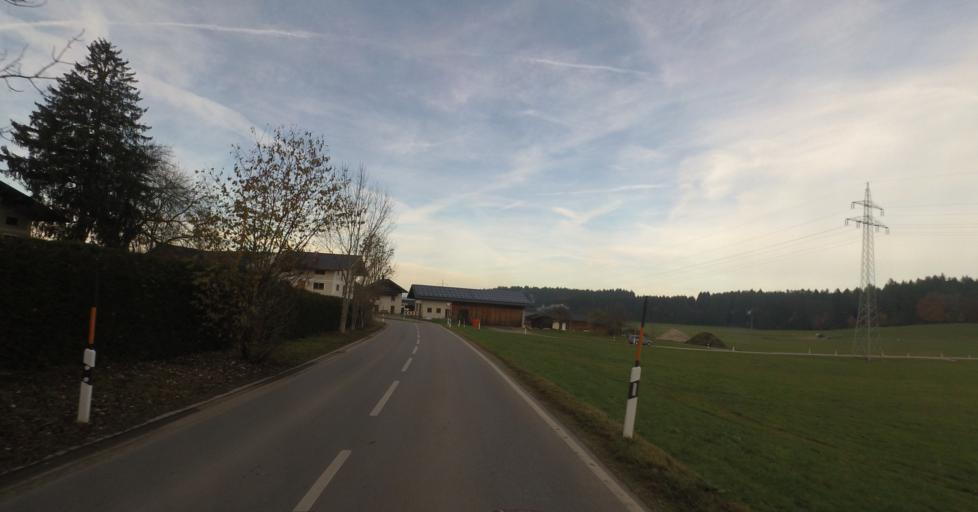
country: DE
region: Bavaria
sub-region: Upper Bavaria
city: Nussdorf
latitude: 47.8874
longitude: 12.6112
